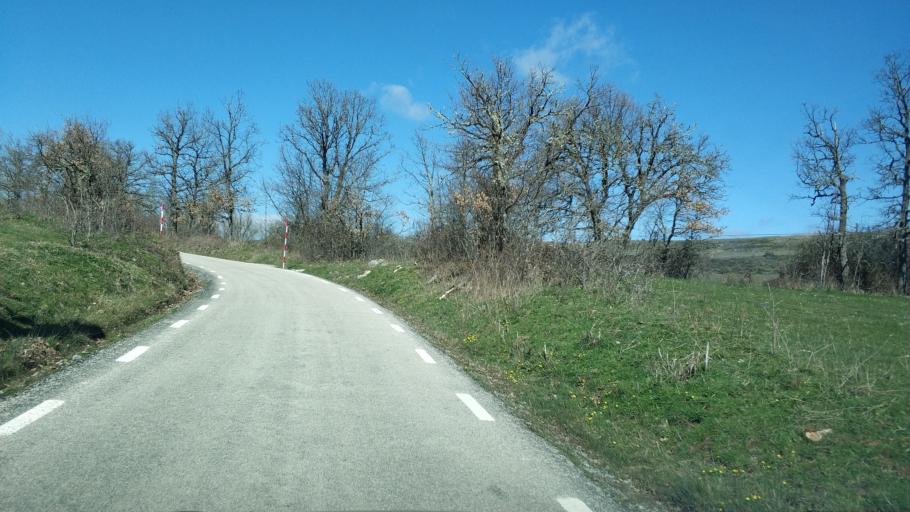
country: ES
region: Cantabria
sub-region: Provincia de Cantabria
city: Mataporquera
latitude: 42.8710
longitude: -4.0821
